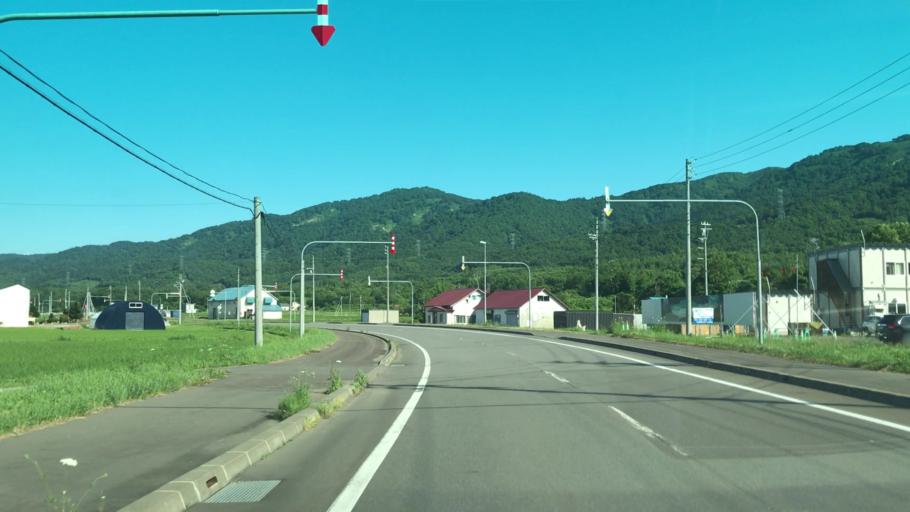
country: JP
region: Hokkaido
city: Yoichi
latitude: 43.0396
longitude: 140.7347
